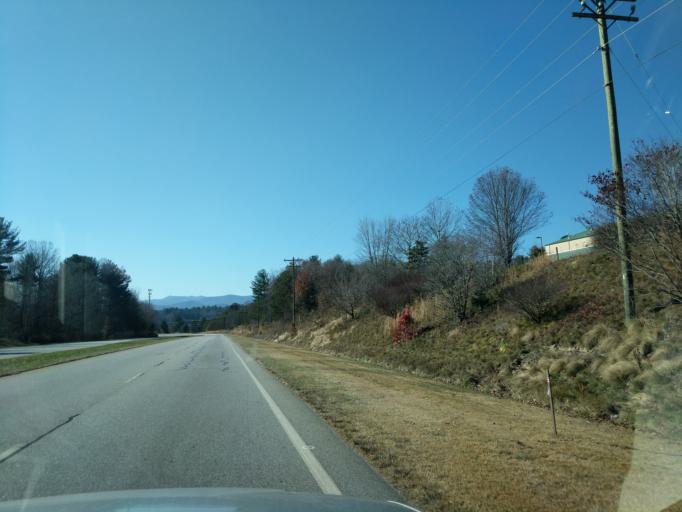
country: US
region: North Carolina
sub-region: Henderson County
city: Mills River
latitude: 35.4057
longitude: -82.5621
